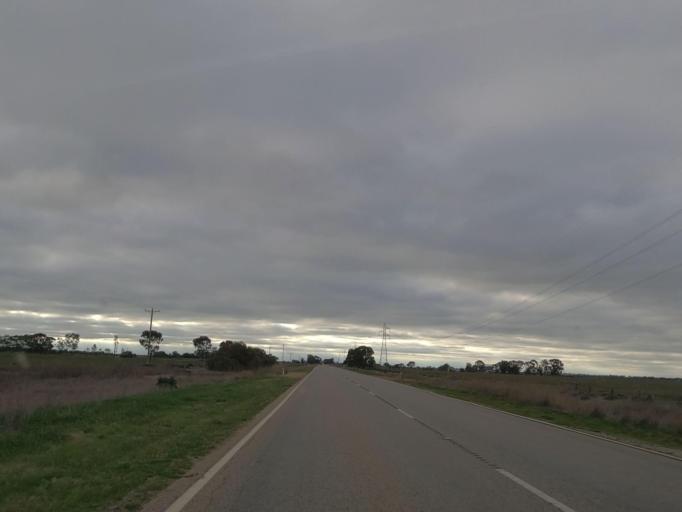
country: AU
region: Victoria
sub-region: Swan Hill
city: Swan Hill
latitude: -35.8903
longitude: 143.9428
